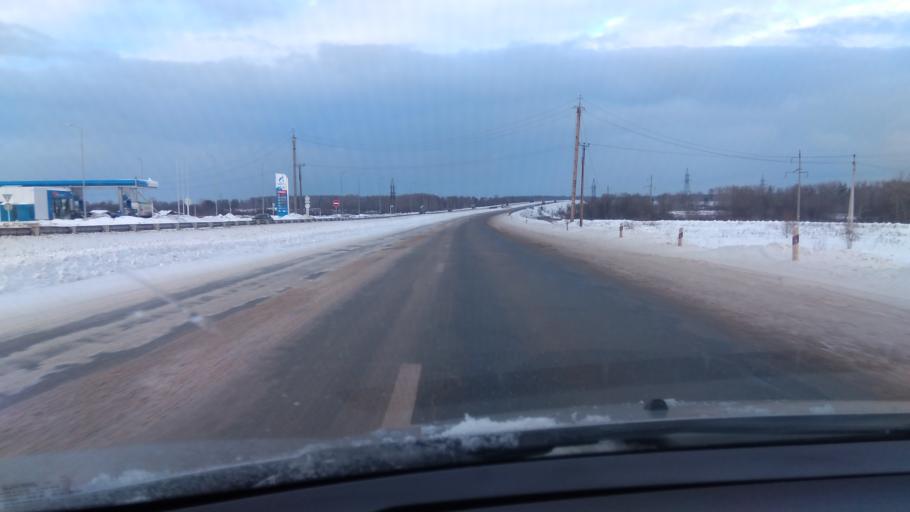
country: RU
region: Sverdlovsk
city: Tsementnyy
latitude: 57.4968
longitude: 60.1751
